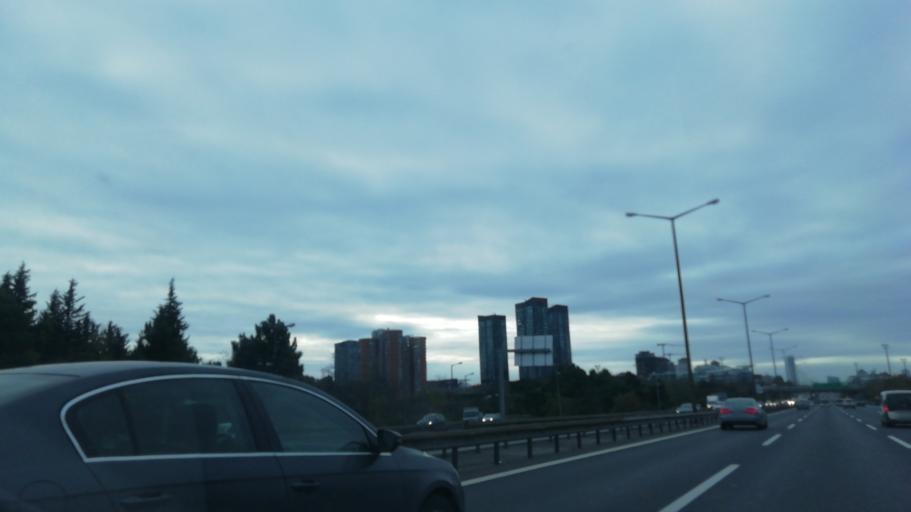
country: TR
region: Istanbul
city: Umraniye
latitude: 41.0345
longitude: 29.1209
